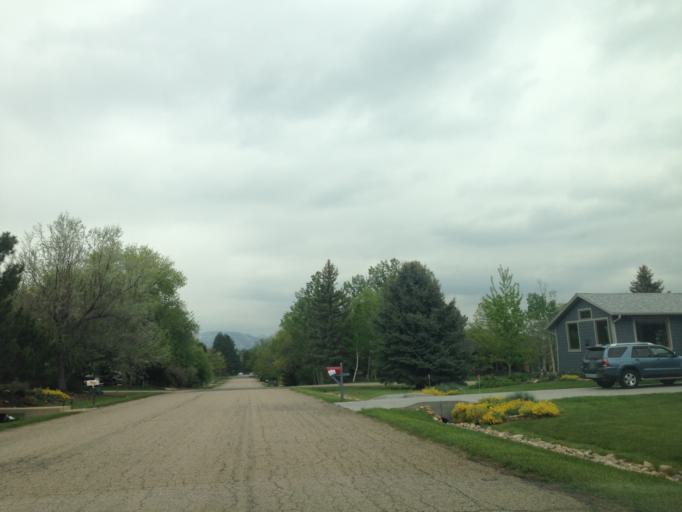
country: US
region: Colorado
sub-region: Boulder County
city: Louisville
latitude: 40.0068
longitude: -105.1704
